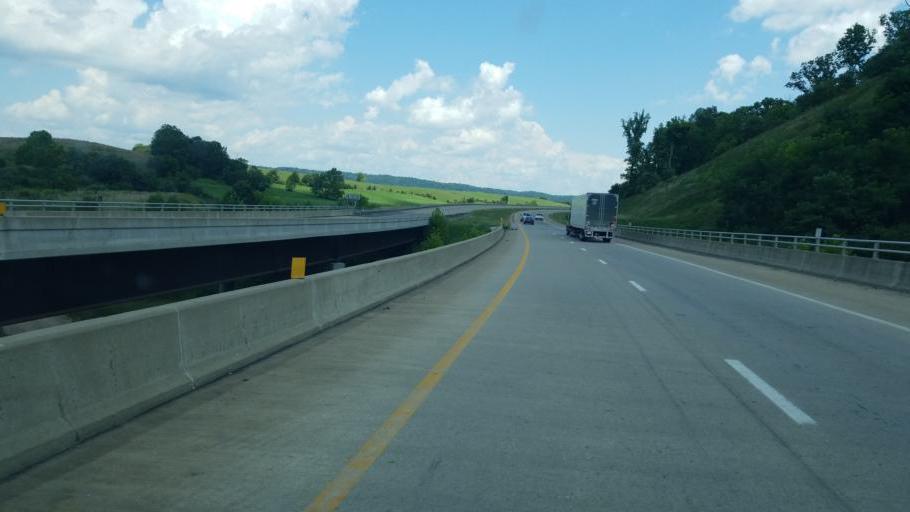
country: US
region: West Virginia
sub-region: Mason County
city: Point Pleasant
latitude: 38.7705
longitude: -82.0490
